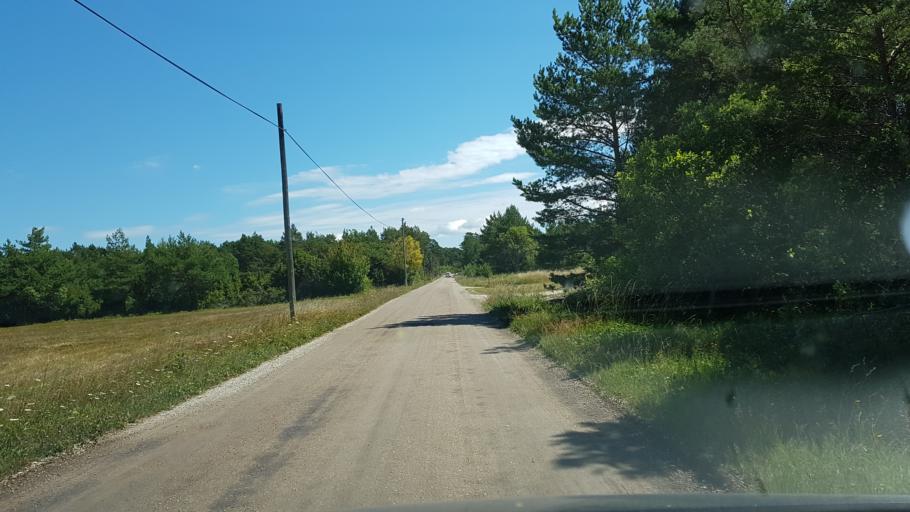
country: SE
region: Gotland
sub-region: Gotland
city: Visby
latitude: 57.8033
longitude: 18.5015
